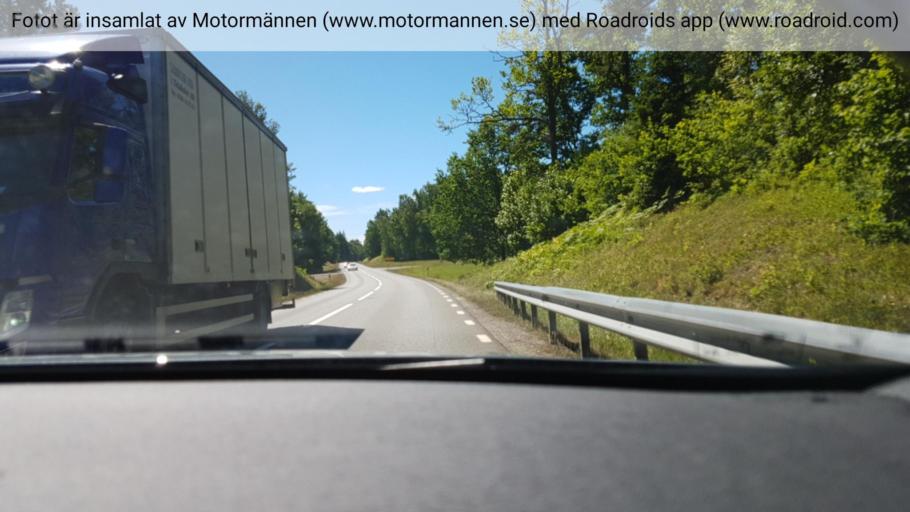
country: SE
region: Joenkoeping
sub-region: Mullsjo Kommun
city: Mullsjoe
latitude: 57.8244
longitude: 13.8509
